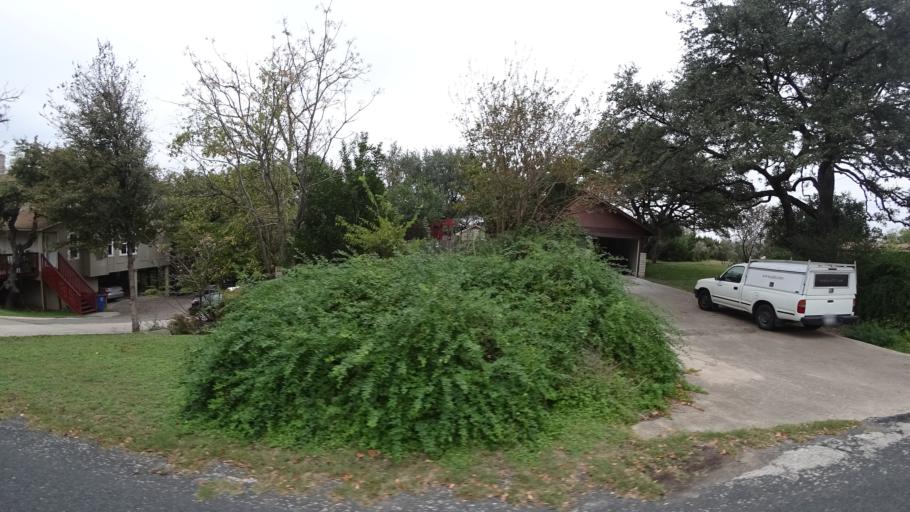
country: US
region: Texas
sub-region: Travis County
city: Barton Creek
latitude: 30.2436
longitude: -97.8877
